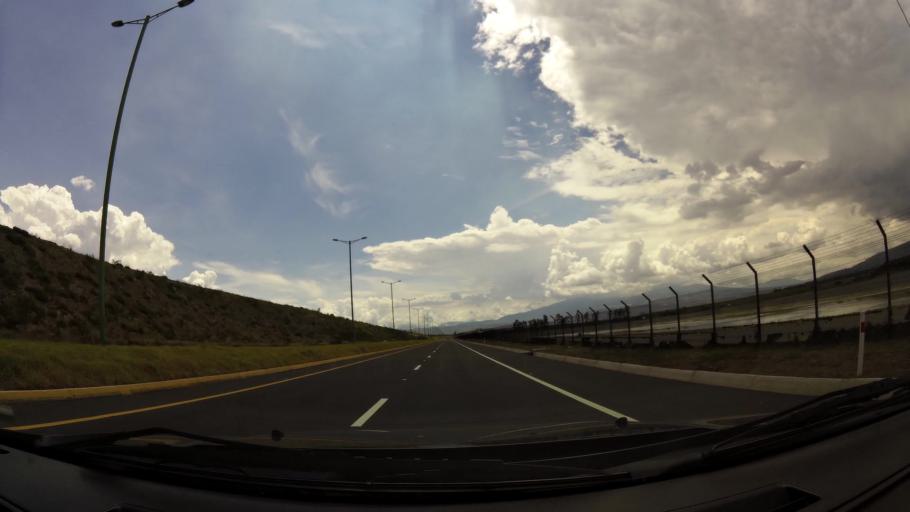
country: EC
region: Pichincha
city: Quito
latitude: -0.1115
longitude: -78.3656
